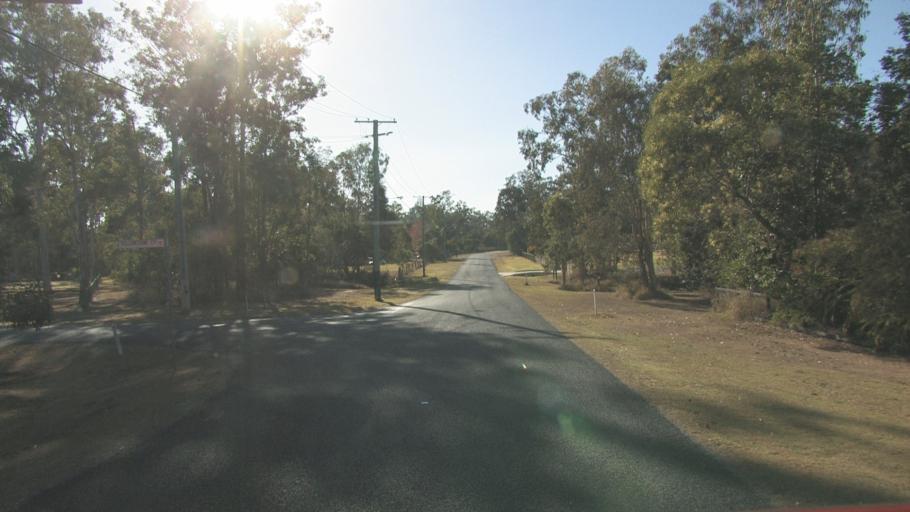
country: AU
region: Queensland
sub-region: Logan
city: North Maclean
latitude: -27.7479
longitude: 153.0099
